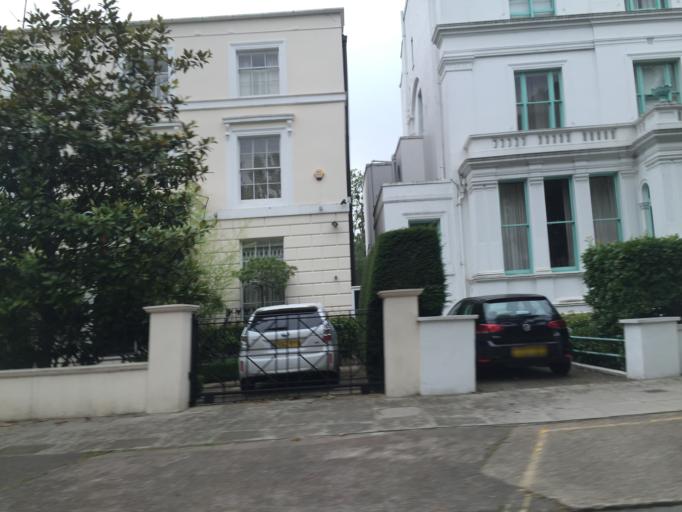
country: GB
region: England
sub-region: Greater London
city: Belsize Park
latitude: 51.5309
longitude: -0.1818
